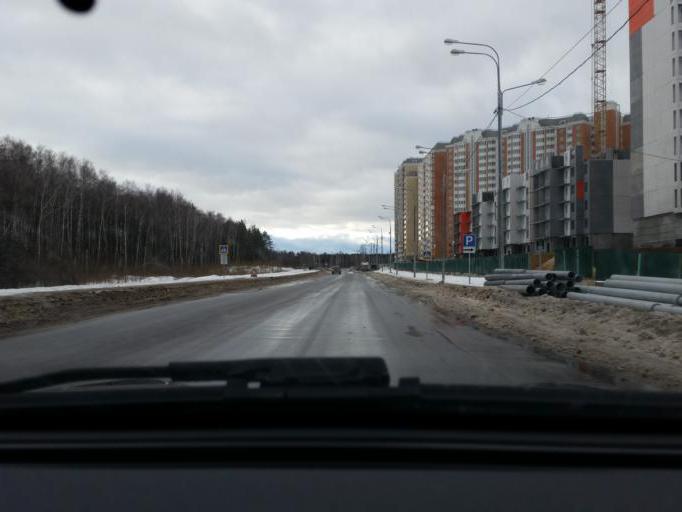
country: RU
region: Moskovskaya
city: Shcherbinka
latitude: 55.5247
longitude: 37.6002
